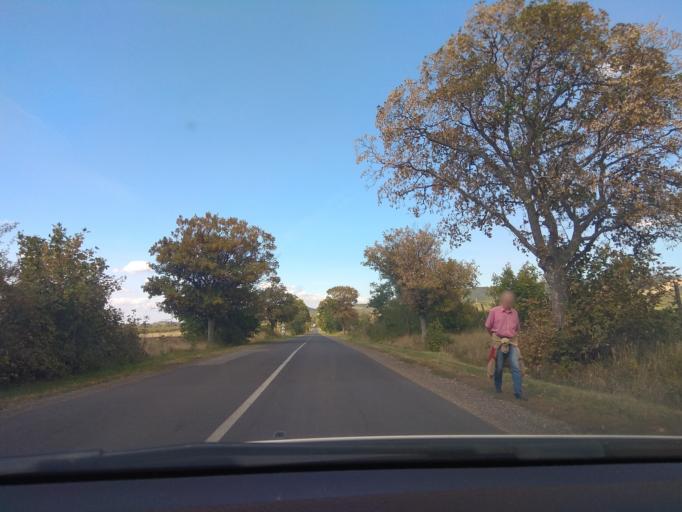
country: HU
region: Borsod-Abauj-Zemplen
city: Tallya
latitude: 48.2183
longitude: 21.2430
